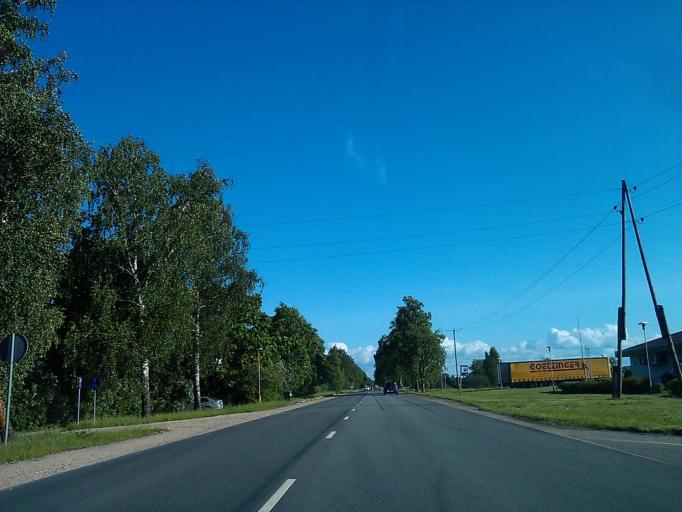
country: LV
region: Adazi
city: Adazi
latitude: 57.0908
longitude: 24.3145
